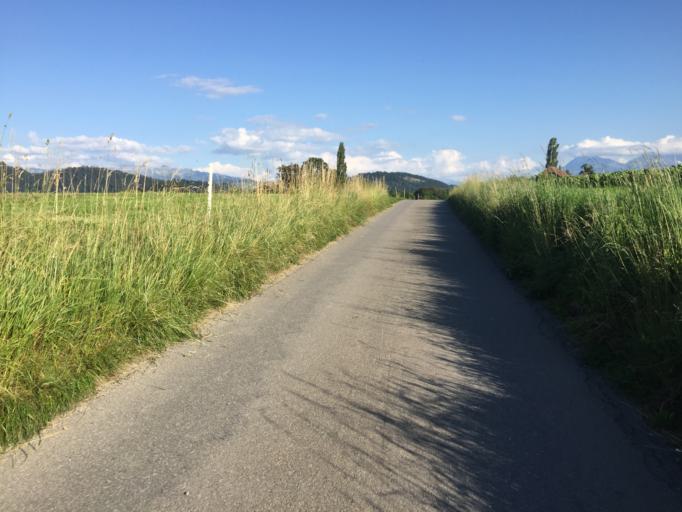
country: CH
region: Bern
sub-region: Bern-Mittelland District
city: Niederwichtrach
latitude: 46.8289
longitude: 7.5879
